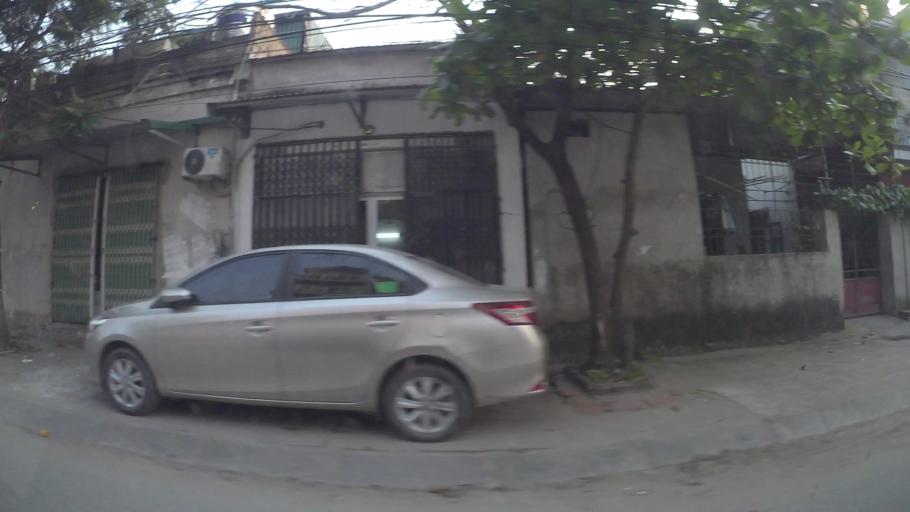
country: VN
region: Ha Noi
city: Van Dien
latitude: 20.9261
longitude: 105.8387
